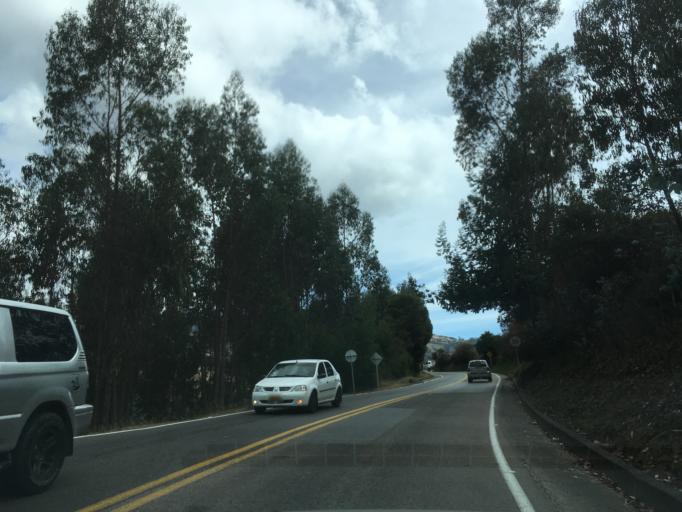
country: CO
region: Boyaca
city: Firavitoba
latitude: 5.6283
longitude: -72.9200
